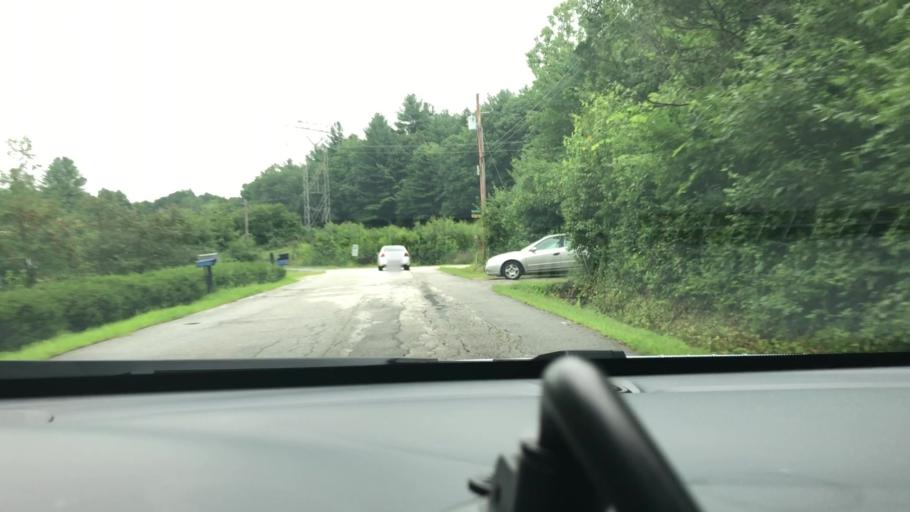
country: US
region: New Hampshire
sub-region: Hillsborough County
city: Pinardville
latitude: 42.9796
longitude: -71.5180
